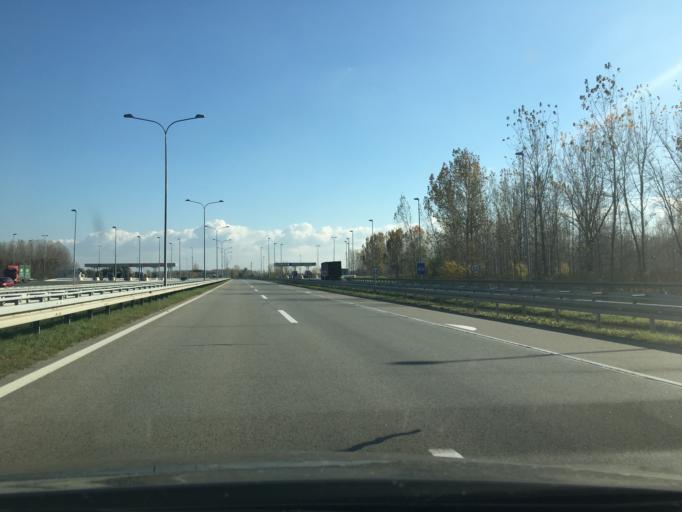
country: RS
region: Autonomna Pokrajina Vojvodina
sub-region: Juznobacki Okrug
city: Petrovaradin
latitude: 45.2894
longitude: 19.8881
